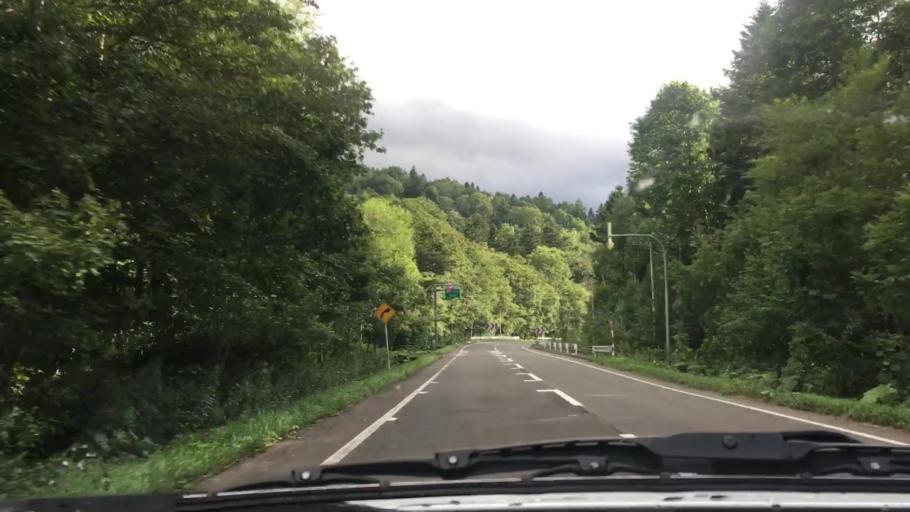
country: JP
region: Hokkaido
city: Shimo-furano
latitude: 43.0878
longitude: 142.6795
